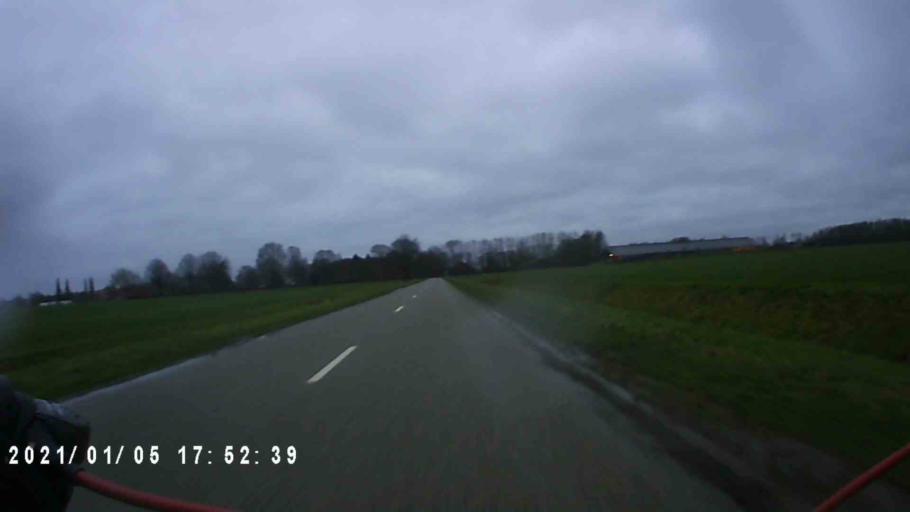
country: NL
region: Groningen
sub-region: Gemeente Slochteren
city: Slochteren
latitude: 53.2039
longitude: 6.8808
